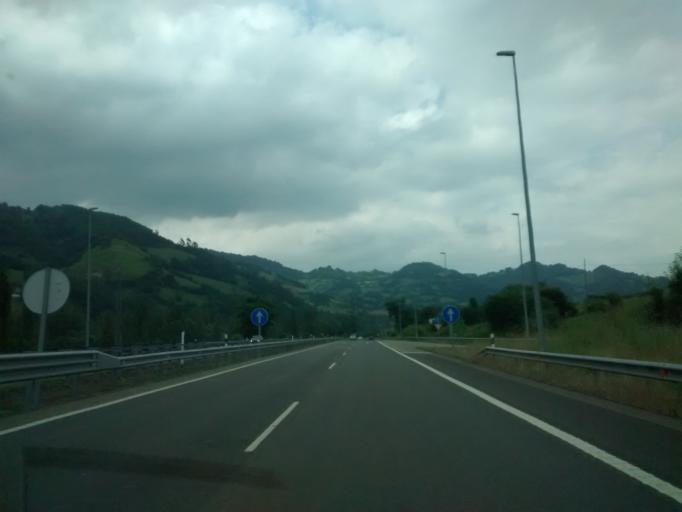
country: ES
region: Asturias
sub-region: Province of Asturias
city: Pola de Lena
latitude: 43.1674
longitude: -5.8253
